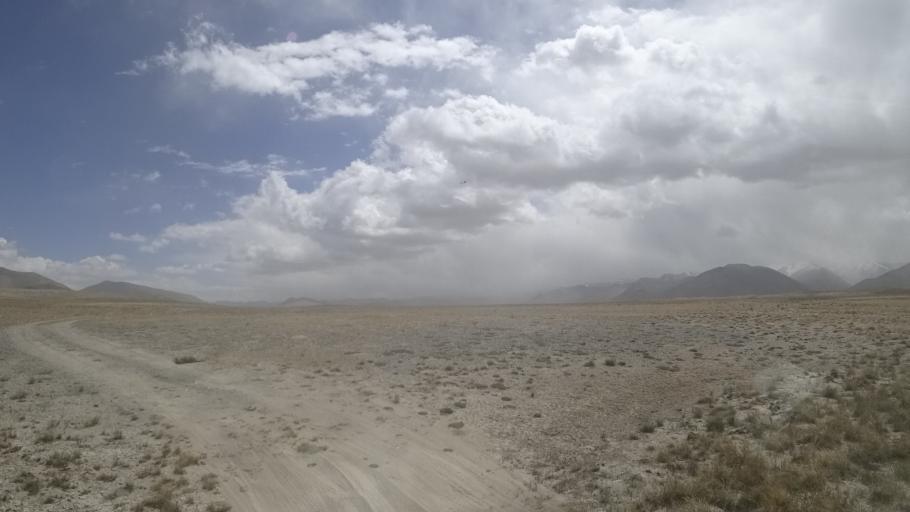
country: TJ
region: Gorno-Badakhshan
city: Murghob
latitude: 37.4730
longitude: 73.9688
